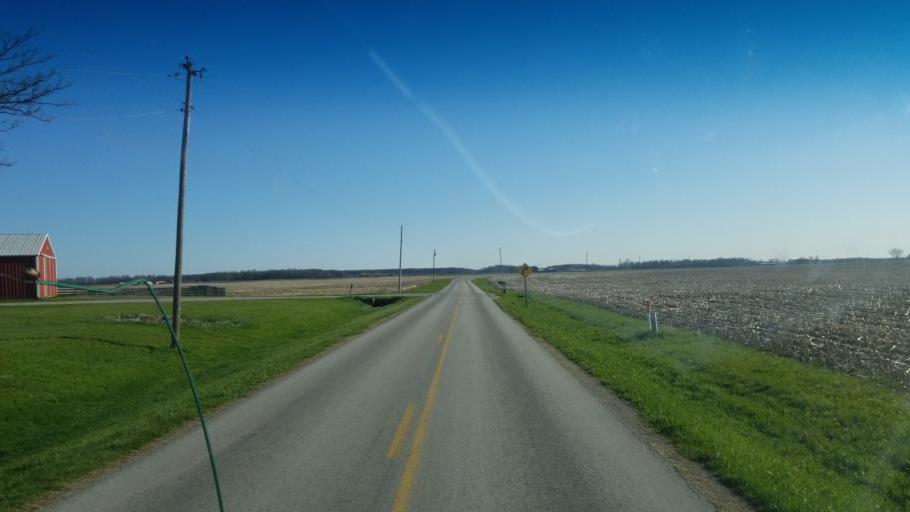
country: US
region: Ohio
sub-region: Hardin County
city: Kenton
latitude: 40.5350
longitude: -83.6212
